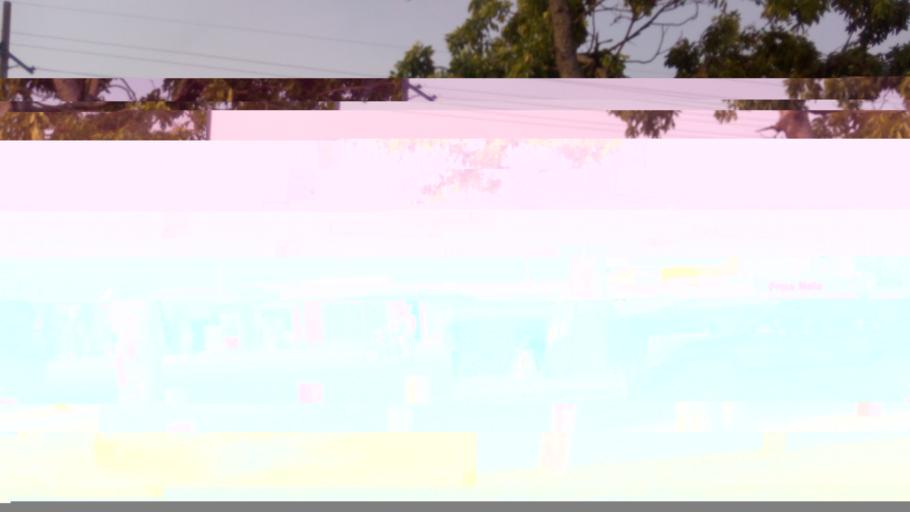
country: BJ
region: Littoral
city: Cotonou
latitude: 6.3764
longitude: 2.4019
